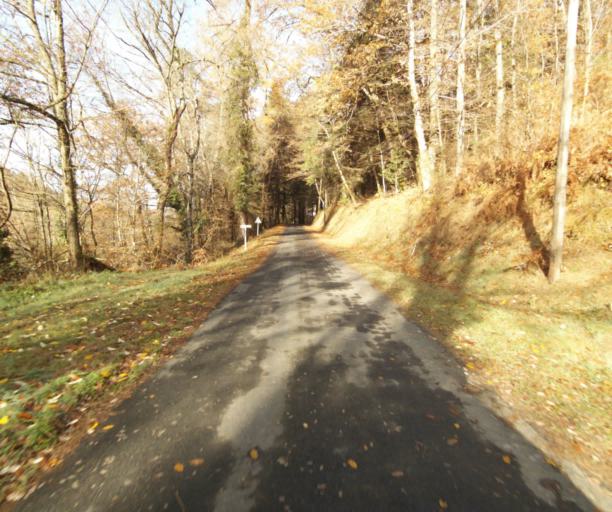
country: FR
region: Limousin
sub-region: Departement de la Correze
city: Sainte-Fortunade
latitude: 45.2162
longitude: 1.7469
